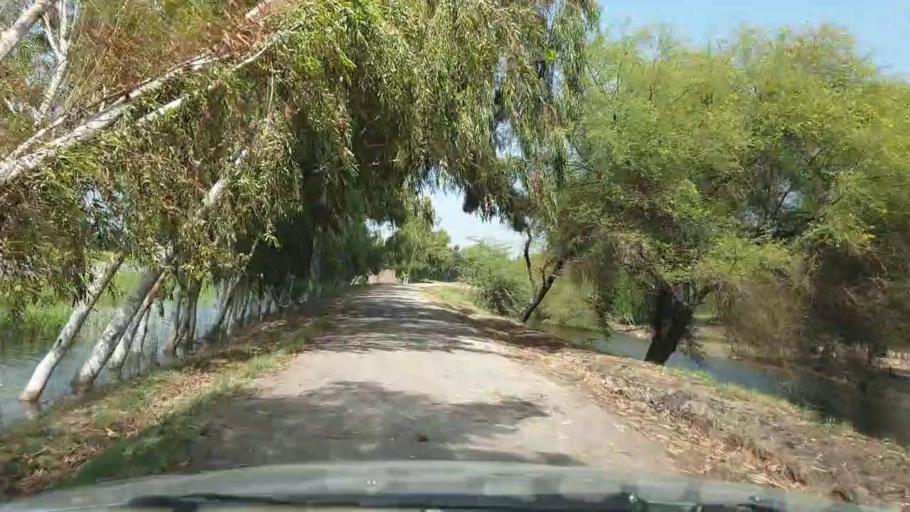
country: PK
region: Sindh
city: Rajo Khanani
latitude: 25.0376
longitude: 68.9364
